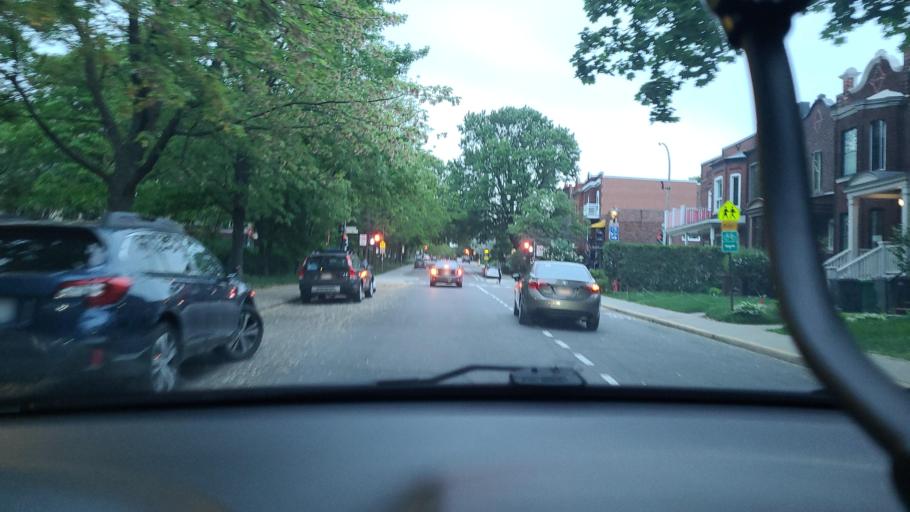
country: CA
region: Quebec
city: Saint-Raymond
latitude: 45.4746
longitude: -73.6178
